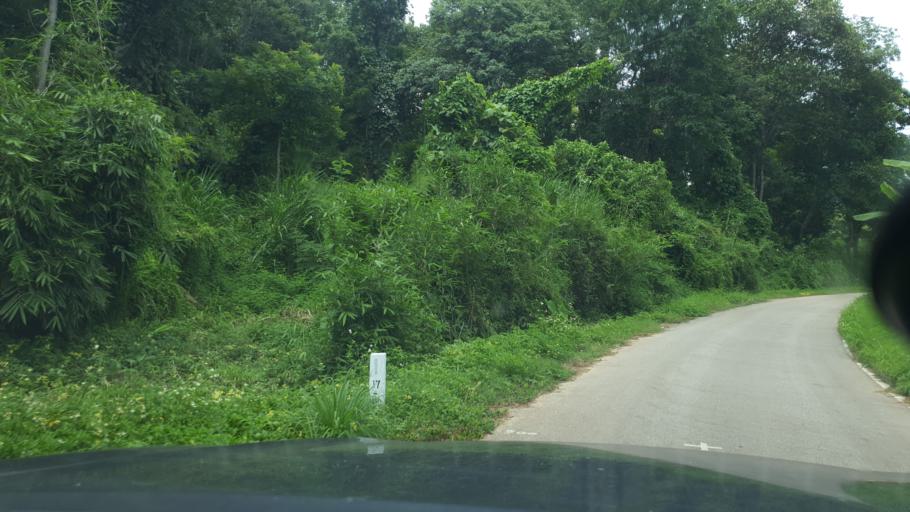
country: TH
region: Lampang
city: Hang Chat
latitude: 18.4218
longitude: 99.2634
